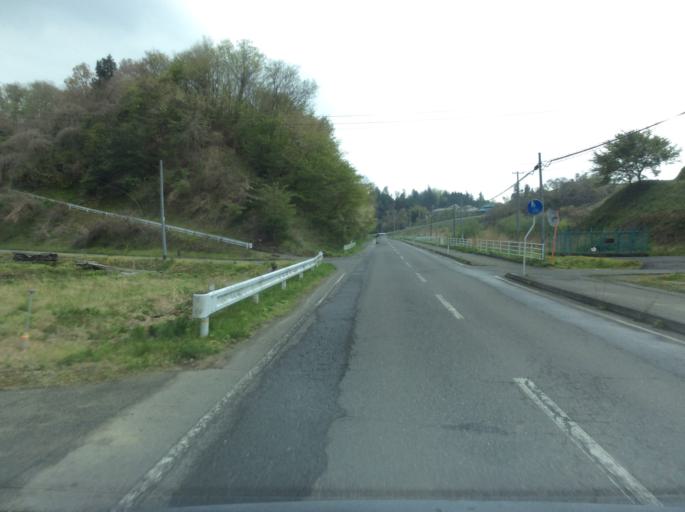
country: JP
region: Fukushima
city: Funehikimachi-funehiki
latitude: 37.4042
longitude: 140.5396
